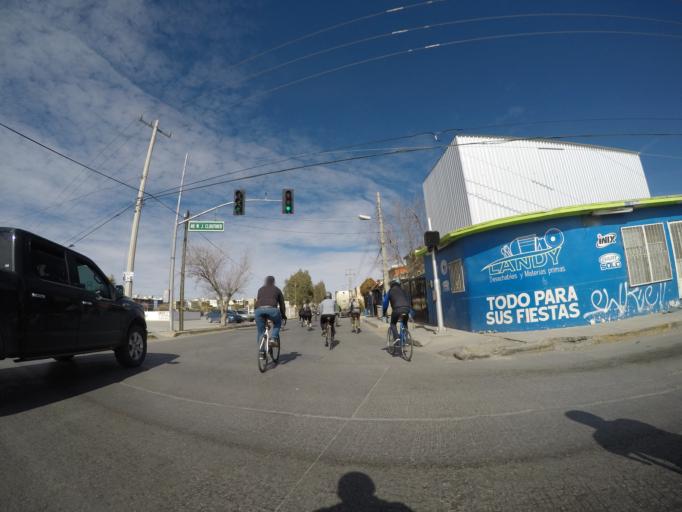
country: US
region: Texas
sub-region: El Paso County
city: Socorro
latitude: 31.6657
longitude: -106.4011
